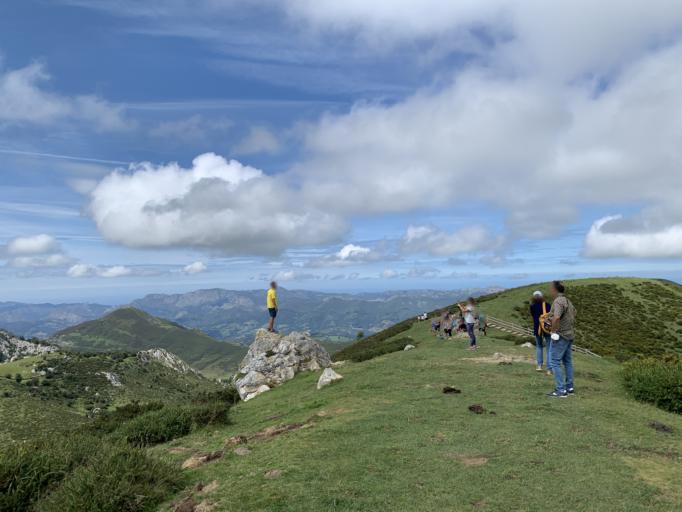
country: ES
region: Asturias
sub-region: Province of Asturias
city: Amieva
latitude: 43.2716
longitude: -4.9846
